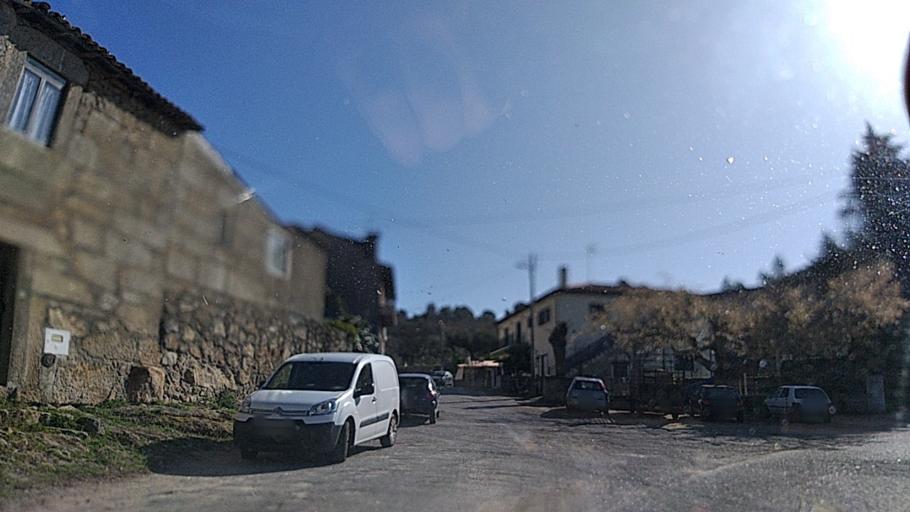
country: PT
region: Guarda
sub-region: Celorico da Beira
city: Celorico da Beira
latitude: 40.6865
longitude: -7.3987
